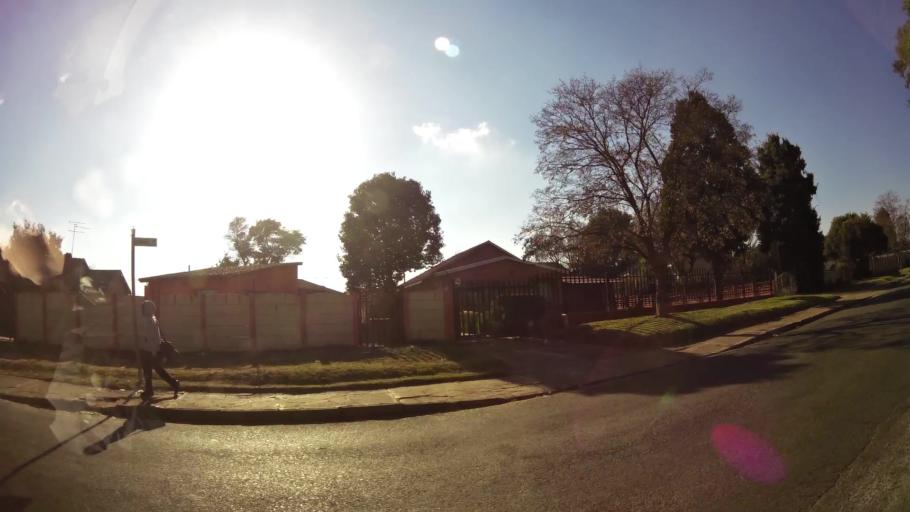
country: ZA
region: Gauteng
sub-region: City of Johannesburg Metropolitan Municipality
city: Roodepoort
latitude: -26.1571
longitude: 27.8579
